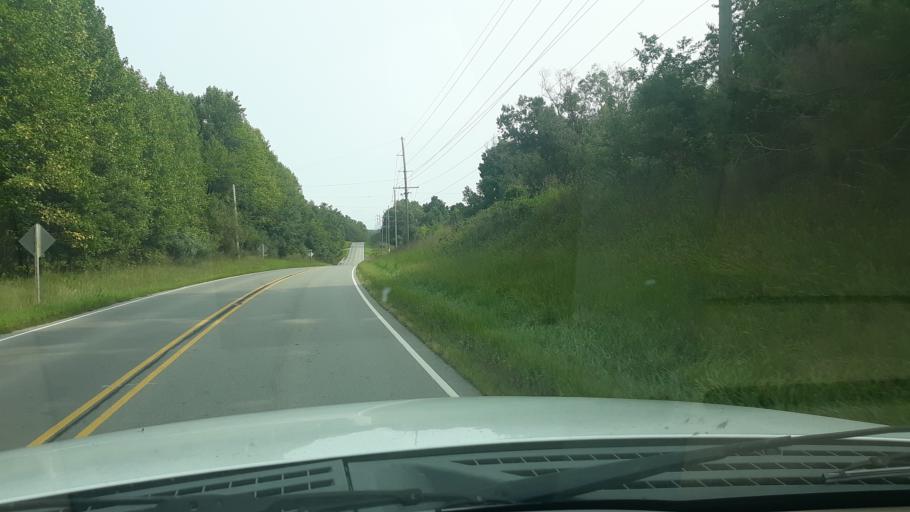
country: US
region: Illinois
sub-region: White County
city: Norris City
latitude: 37.9244
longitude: -88.3508
